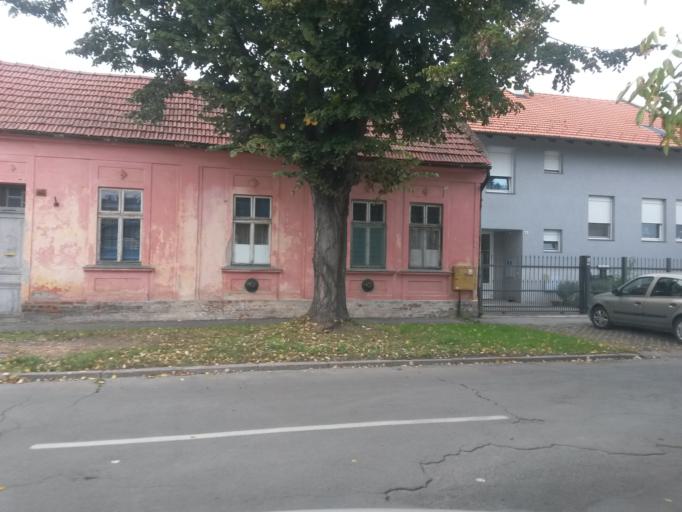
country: HR
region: Osjecko-Baranjska
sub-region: Grad Osijek
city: Osijek
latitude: 45.5501
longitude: 18.6858
